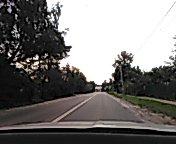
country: RU
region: Moskovskaya
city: Skhodnya
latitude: 55.9429
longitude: 37.2871
